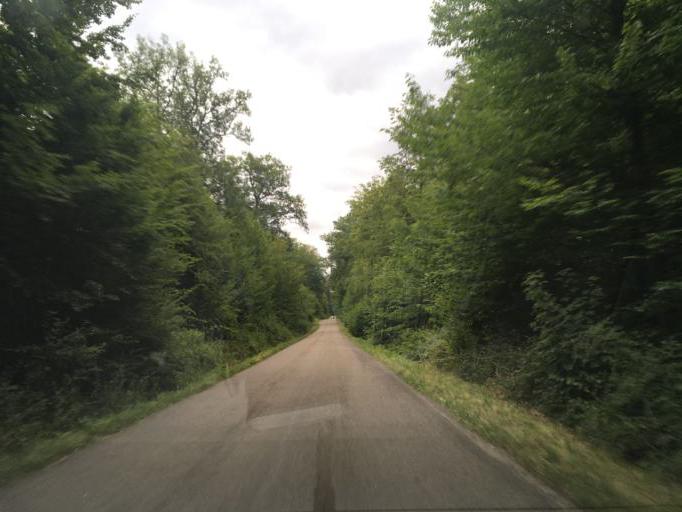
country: DE
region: Baden-Wuerttemberg
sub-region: Tuebingen Region
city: Dettenhausen
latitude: 48.5647
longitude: 9.1058
